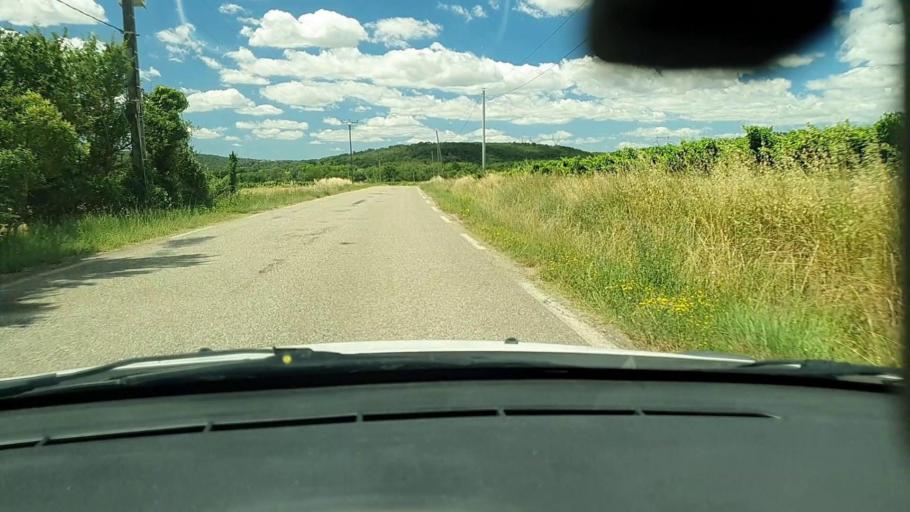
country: FR
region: Languedoc-Roussillon
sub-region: Departement du Gard
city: Blauzac
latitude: 43.9505
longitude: 4.3933
